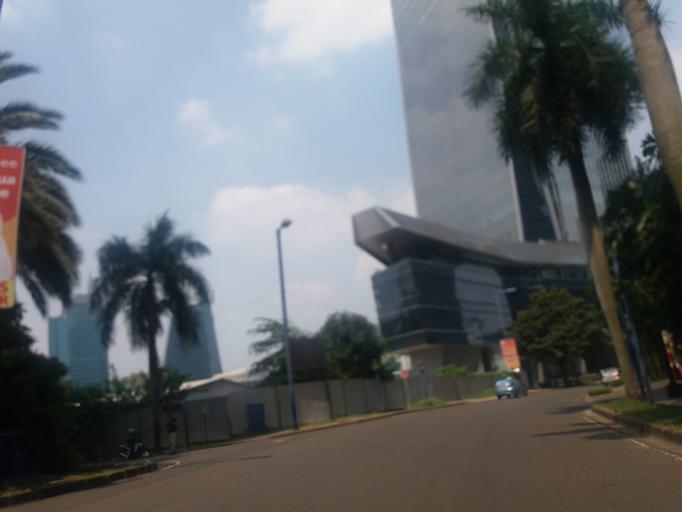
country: ID
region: Jakarta Raya
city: Jakarta
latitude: -6.2285
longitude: 106.8277
